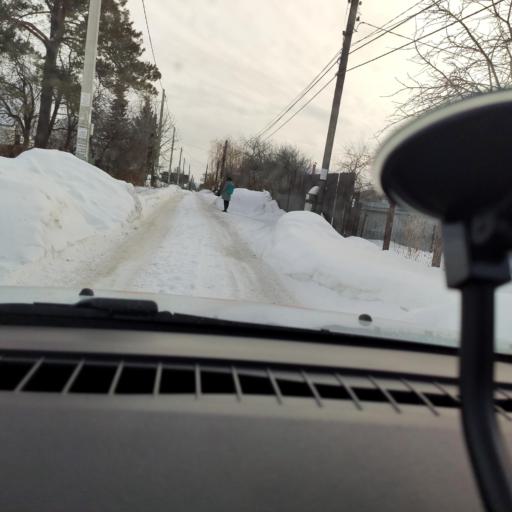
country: RU
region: Samara
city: Petra-Dubrava
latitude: 53.2866
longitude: 50.2960
